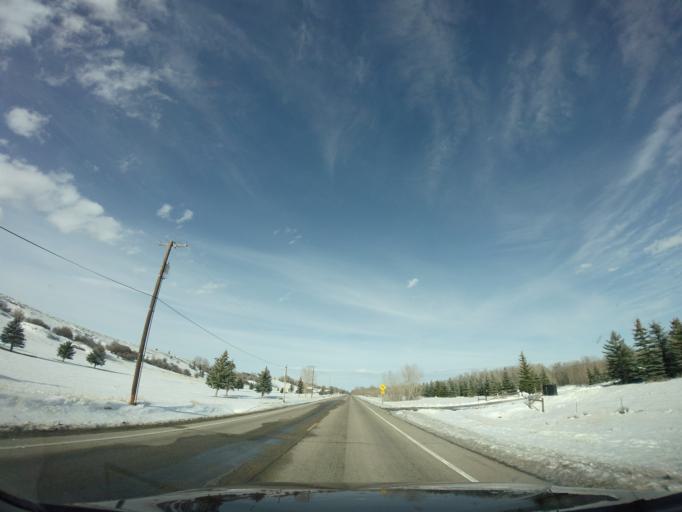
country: US
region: Montana
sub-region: Carbon County
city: Red Lodge
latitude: 45.2066
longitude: -109.2443
